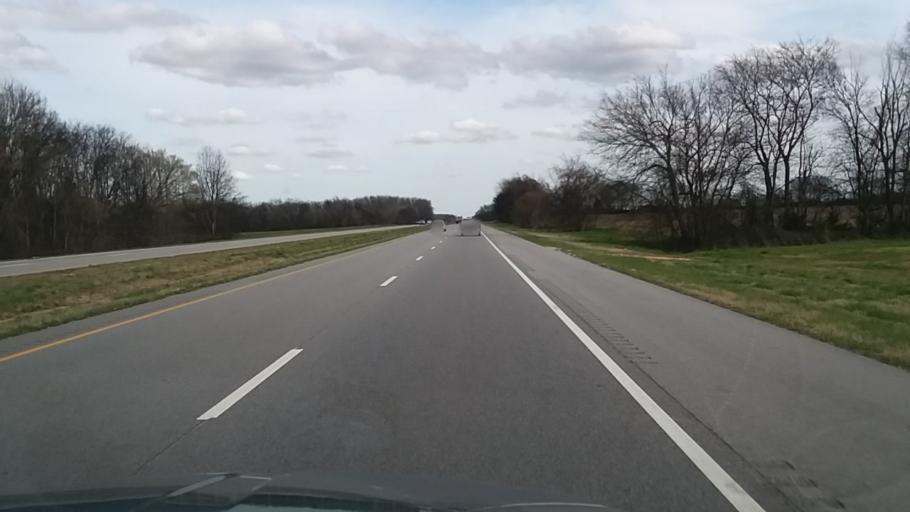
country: US
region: Alabama
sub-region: Lawrence County
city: Town Creek
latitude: 34.6835
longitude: -87.5121
